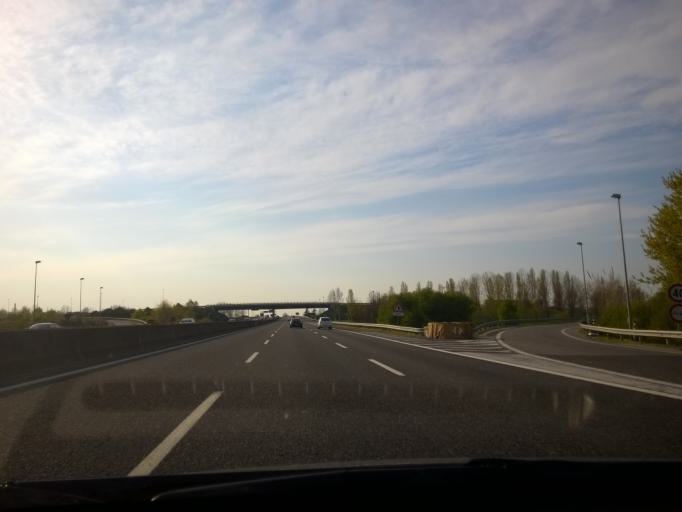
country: IT
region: Emilia-Romagna
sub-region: Forli-Cesena
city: Santa Maria Nuova
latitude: 44.1966
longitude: 12.2218
